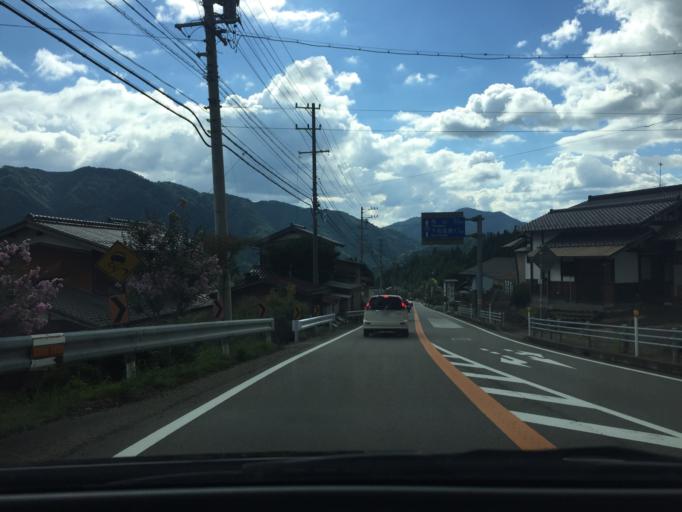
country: JP
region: Gifu
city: Nakatsugawa
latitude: 35.7622
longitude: 137.3189
